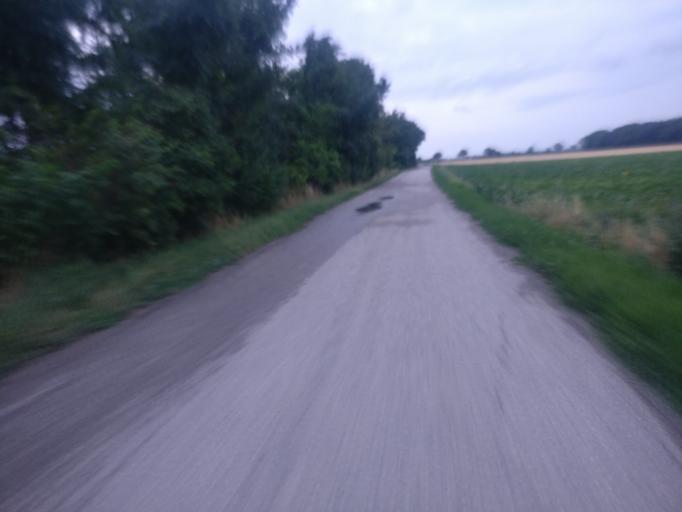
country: AT
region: Lower Austria
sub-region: Politischer Bezirk Modling
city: Guntramsdorf
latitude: 48.0329
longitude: 16.3355
